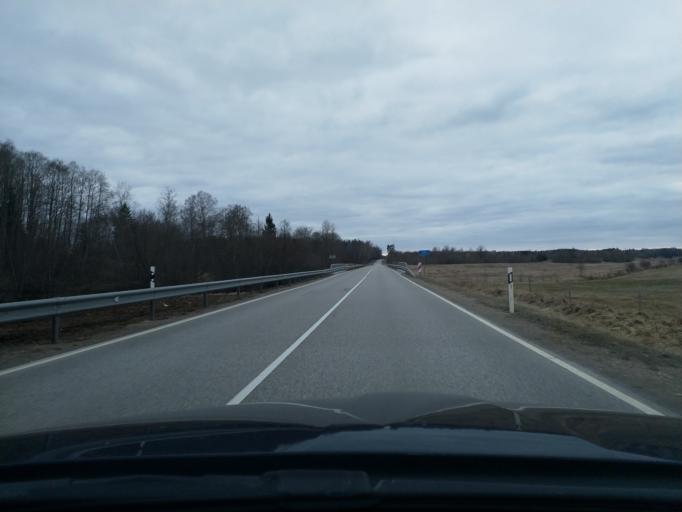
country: LV
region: Kuldigas Rajons
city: Kuldiga
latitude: 56.9662
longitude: 22.0598
